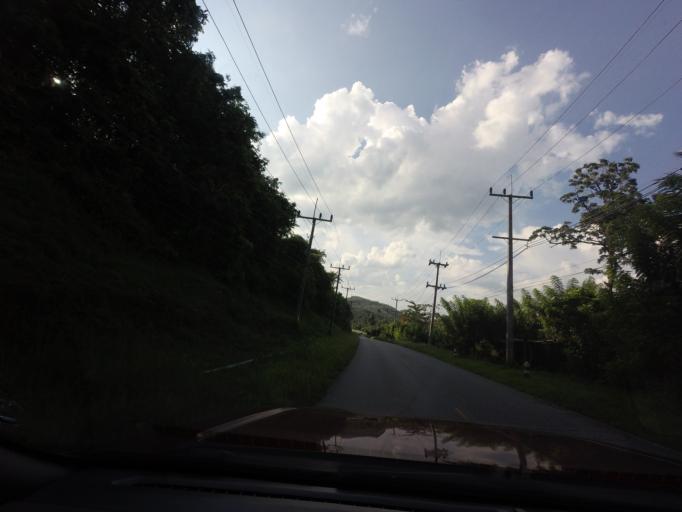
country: TH
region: Yala
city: Ban Nang Sata
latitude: 6.1928
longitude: 101.2599
